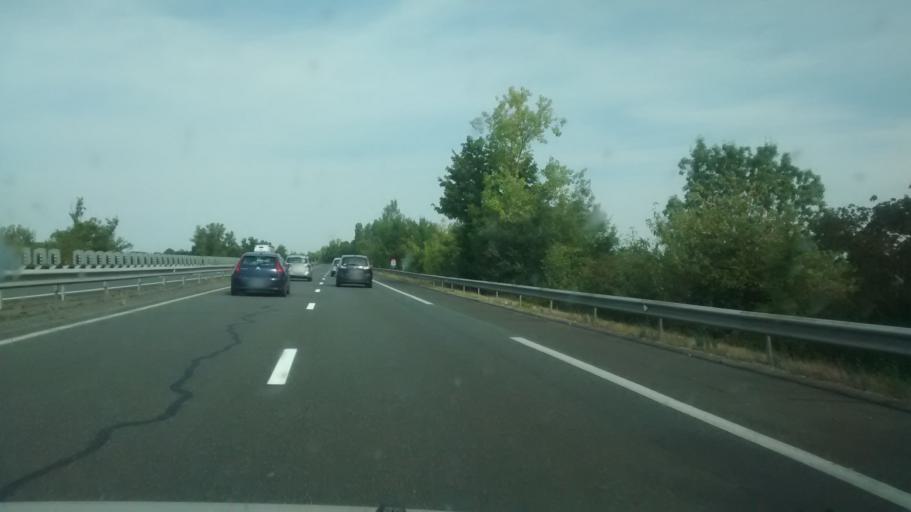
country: FR
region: Aquitaine
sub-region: Departement du Lot-et-Garonne
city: Layrac
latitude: 44.1364
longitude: 0.6731
